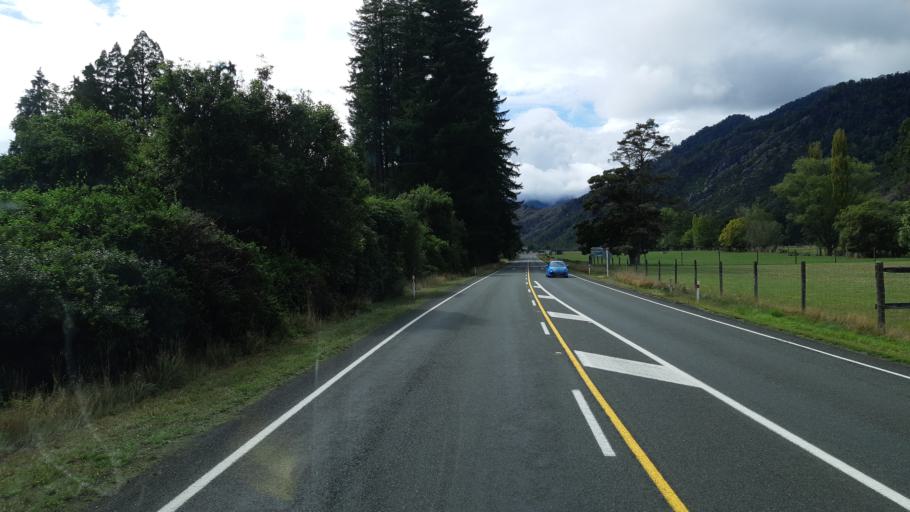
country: NZ
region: West Coast
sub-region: Buller District
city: Westport
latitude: -41.7964
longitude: 172.3412
